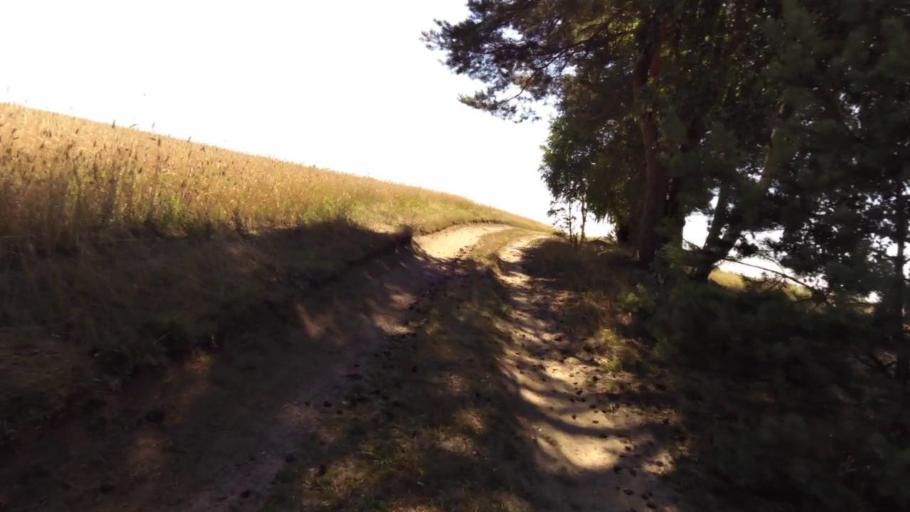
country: PL
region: West Pomeranian Voivodeship
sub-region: Powiat szczecinecki
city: Szczecinek
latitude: 53.8058
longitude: 16.6969
